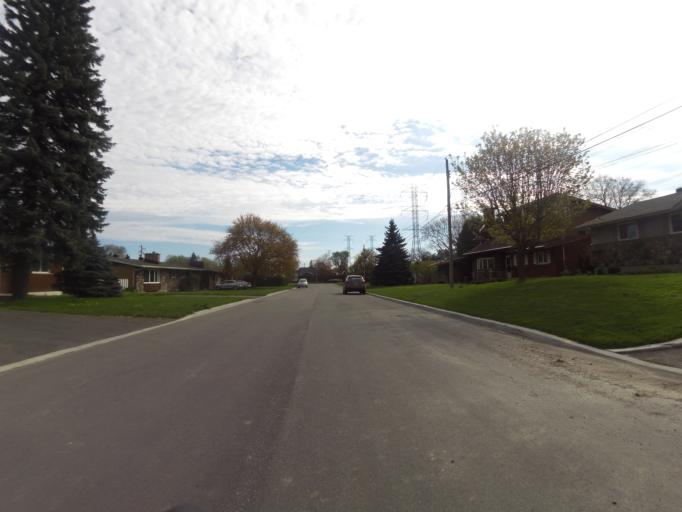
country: CA
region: Ontario
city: Bells Corners
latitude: 45.3286
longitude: -75.7529
